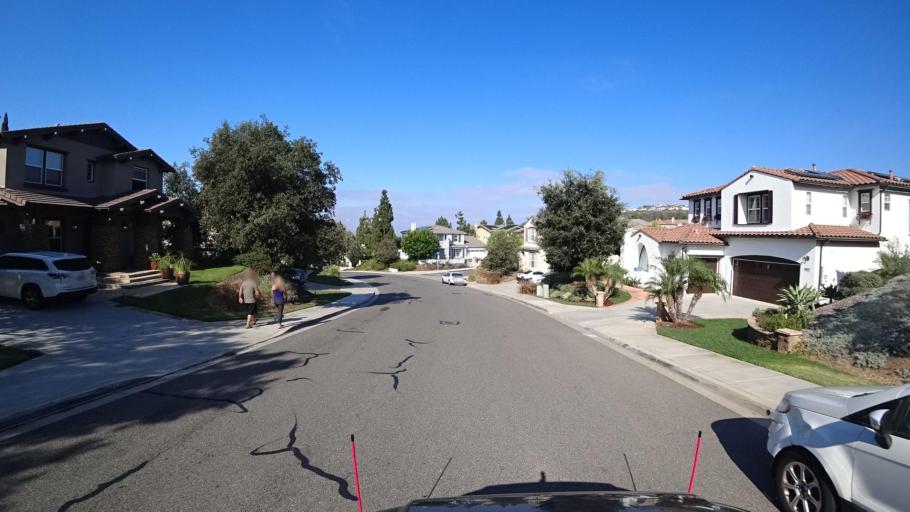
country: US
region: California
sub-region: San Diego County
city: Lake San Marcos
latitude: 33.0997
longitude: -117.1821
